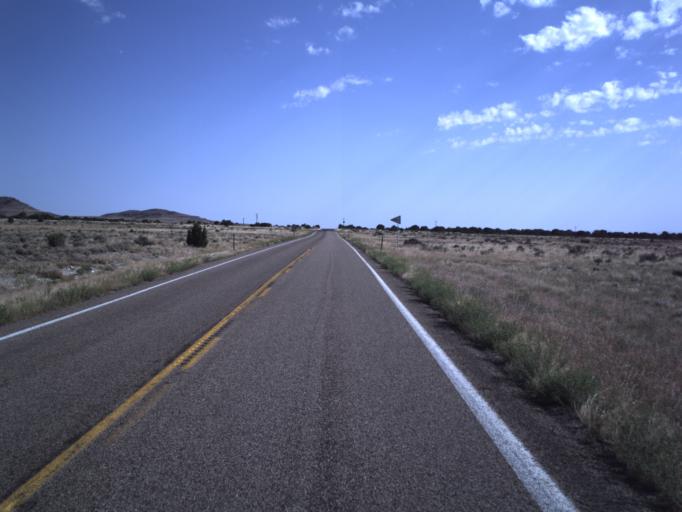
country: US
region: Utah
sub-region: Beaver County
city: Milford
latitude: 38.8298
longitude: -112.8493
